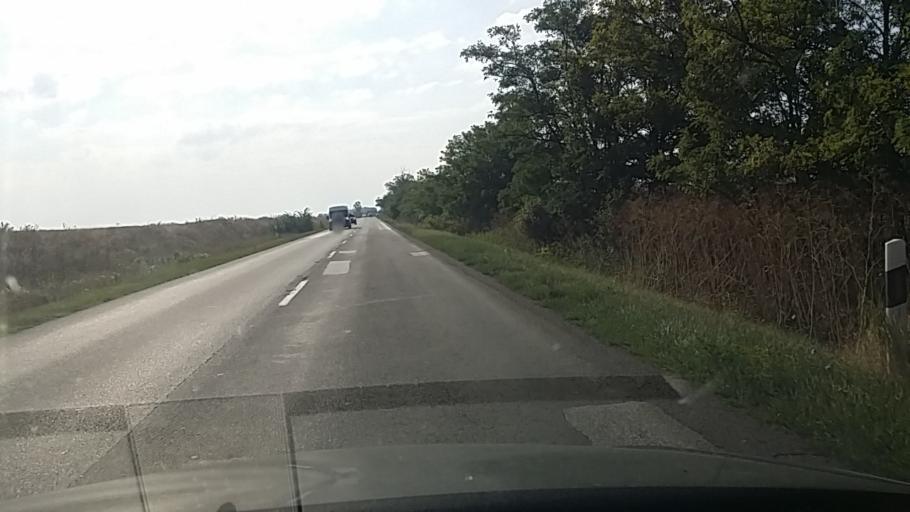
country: HU
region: Jasz-Nagykun-Szolnok
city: Ocsod
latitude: 46.8914
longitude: 20.4360
